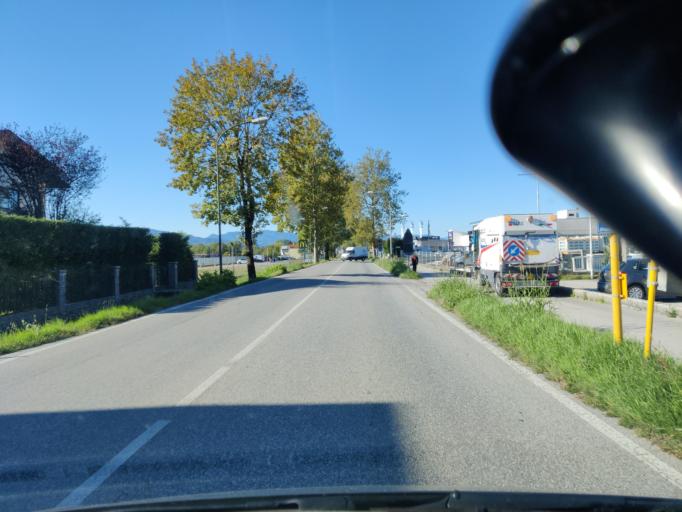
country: IT
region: Veneto
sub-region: Provincia di Belluno
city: Belluno
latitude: 46.1664
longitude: 12.2453
